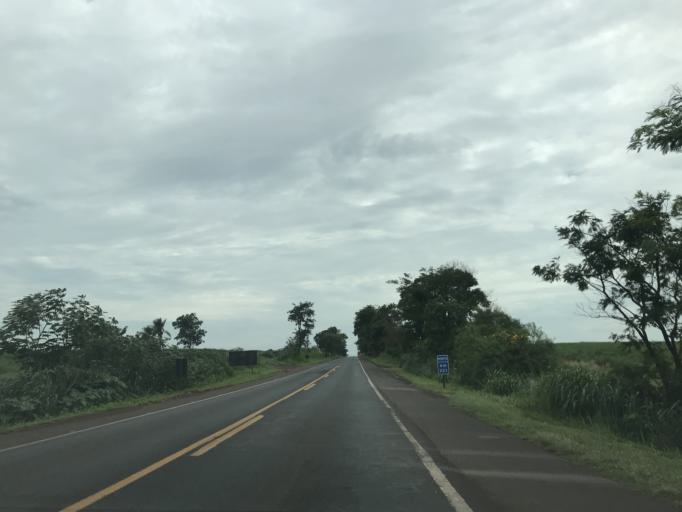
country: BR
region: Minas Gerais
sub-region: Frutal
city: Frutal
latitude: -20.1233
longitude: -49.1042
